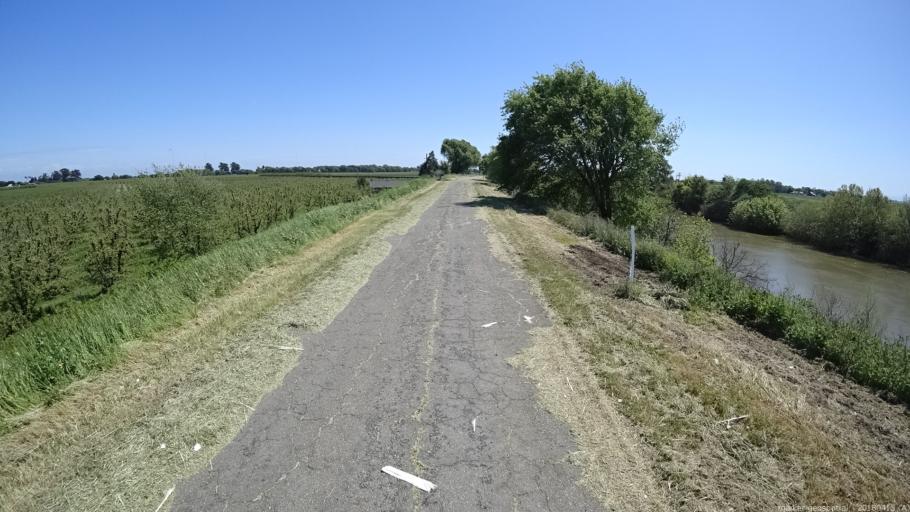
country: US
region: California
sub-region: Sacramento County
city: Walnut Grove
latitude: 38.2828
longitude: -121.6022
